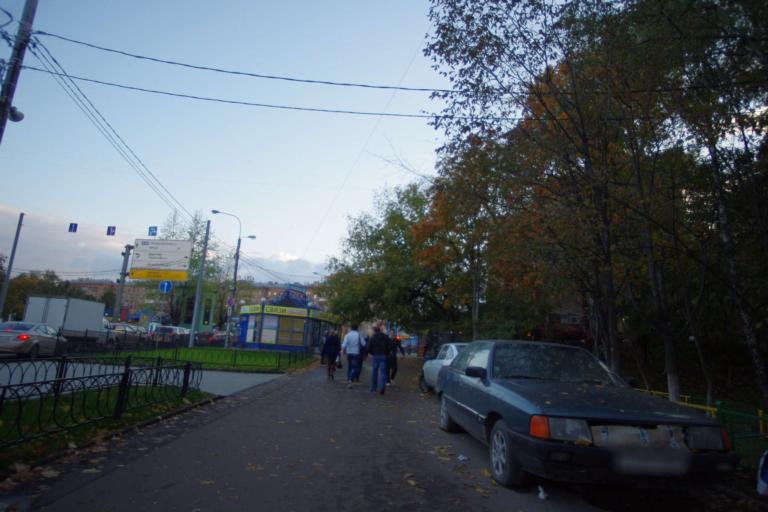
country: RU
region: Moskovskaya
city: Leninskiye Gory
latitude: 55.6894
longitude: 37.5742
